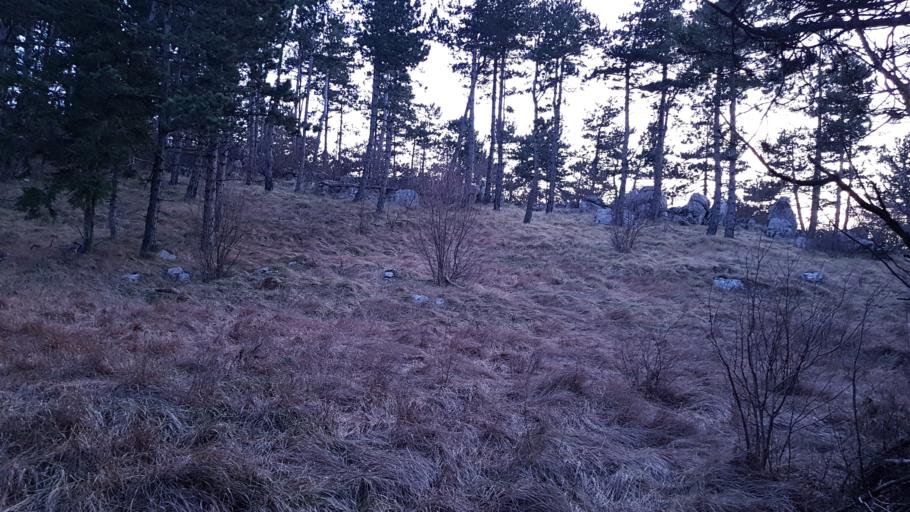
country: SI
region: Kanal
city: Kanal
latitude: 46.0339
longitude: 13.6835
